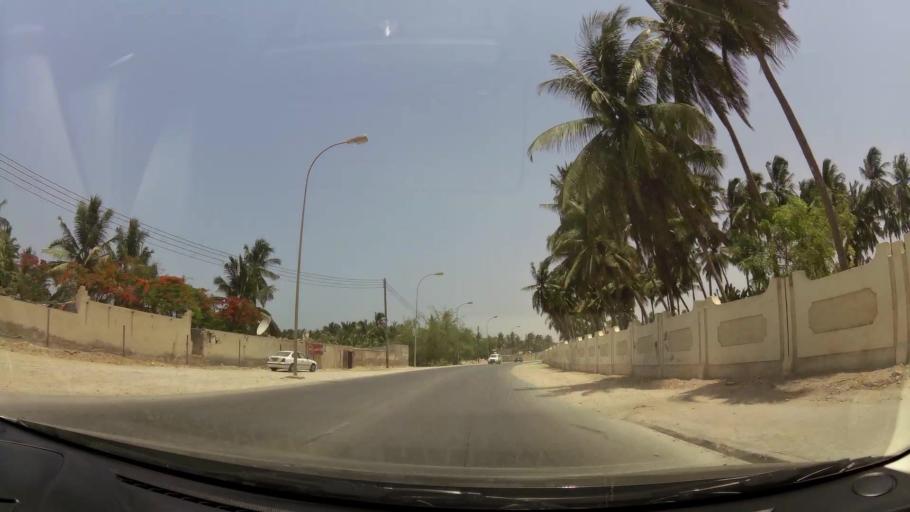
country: OM
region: Zufar
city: Salalah
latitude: 17.0113
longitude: 54.1096
